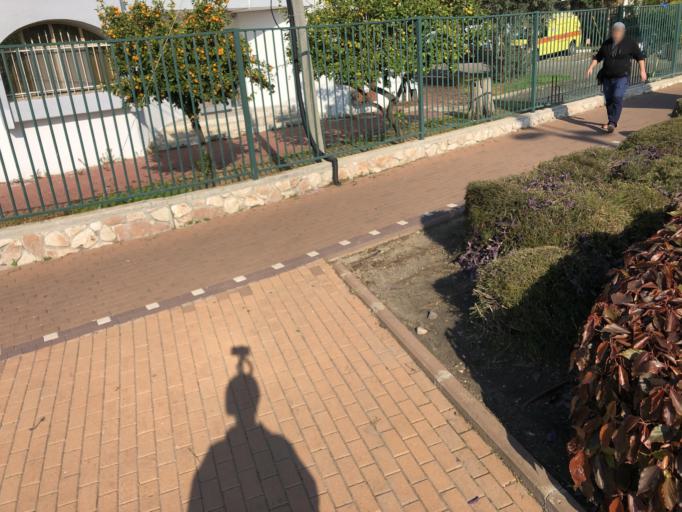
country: IL
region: Northern District
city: `Akko
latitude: 32.9233
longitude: 35.0859
